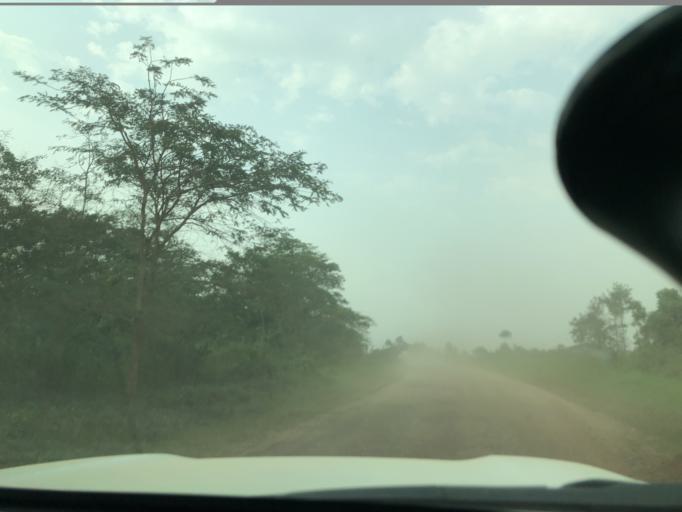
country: UG
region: Western Region
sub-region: Kasese District
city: Margherita
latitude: 0.2576
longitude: 29.6787
